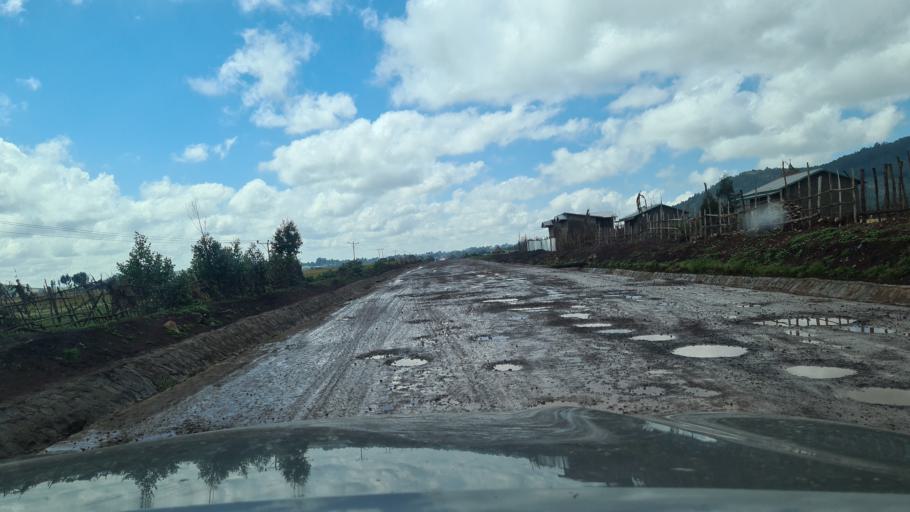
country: ET
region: Oromiya
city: Huruta
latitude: 8.0858
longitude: 39.5411
